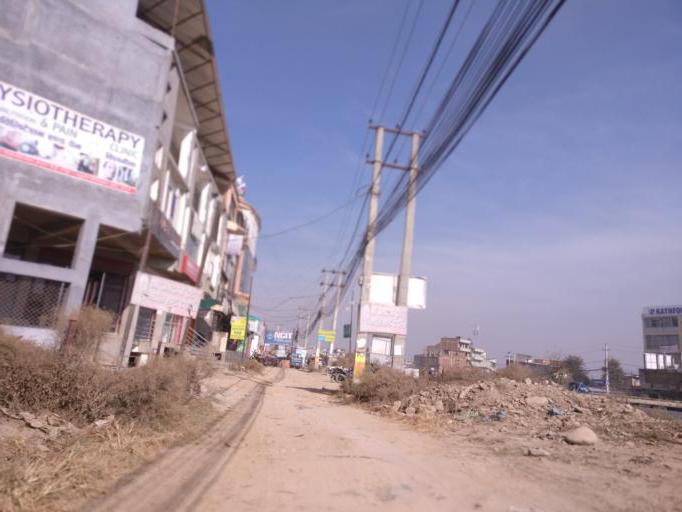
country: NP
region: Central Region
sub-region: Bagmati Zone
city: Patan
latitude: 27.6710
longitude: 85.3390
